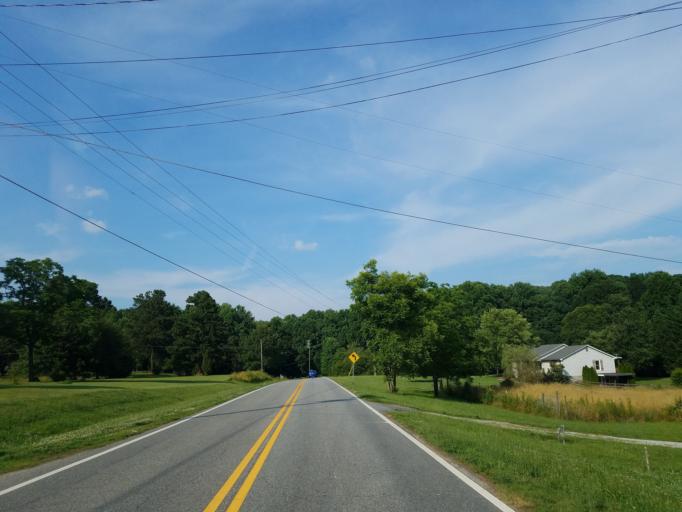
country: US
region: Georgia
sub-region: Forsyth County
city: Cumming
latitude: 34.2847
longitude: -84.0713
